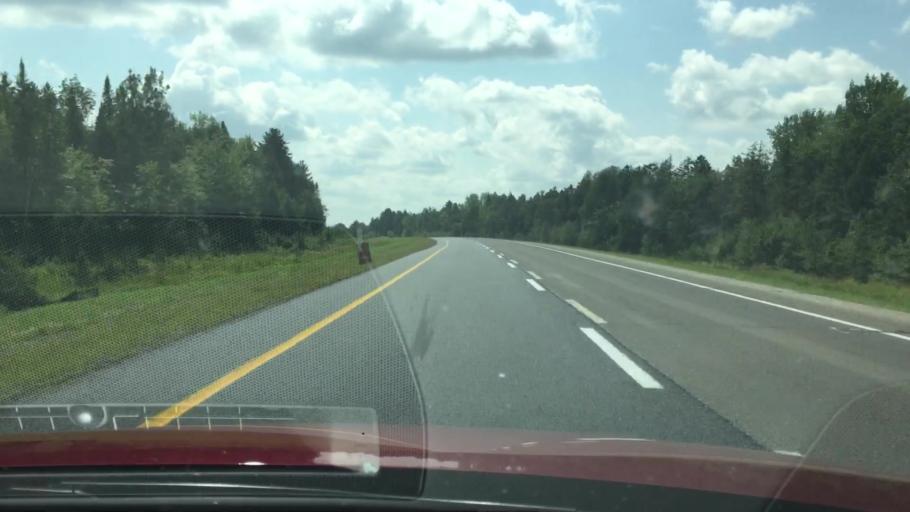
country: US
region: Maine
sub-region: Penobscot County
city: Medway
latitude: 45.7037
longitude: -68.4826
